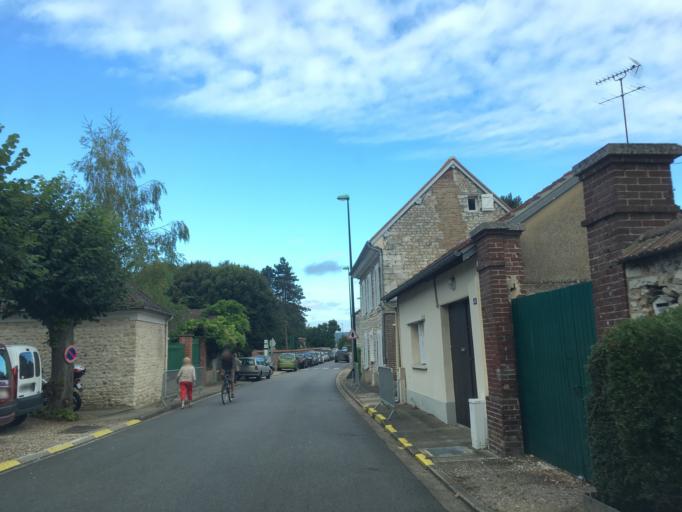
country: FR
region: Haute-Normandie
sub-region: Departement de l'Eure
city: Saint-Just
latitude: 49.1321
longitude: 1.4454
